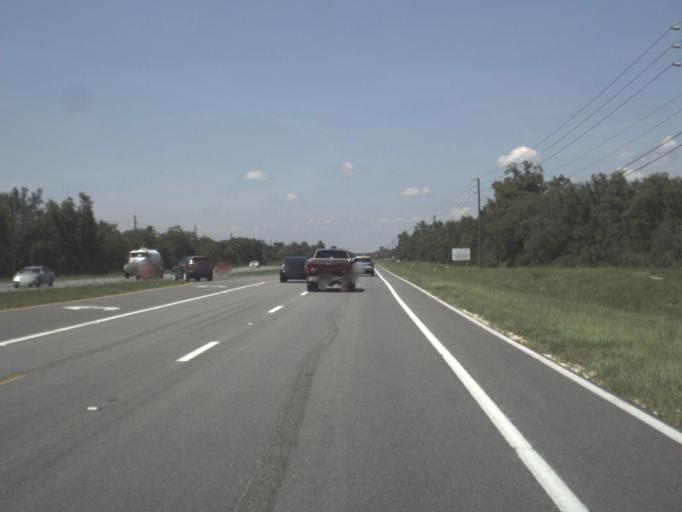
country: US
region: Florida
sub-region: Hernando County
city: North Weeki Wachee
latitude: 28.5716
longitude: -82.5578
